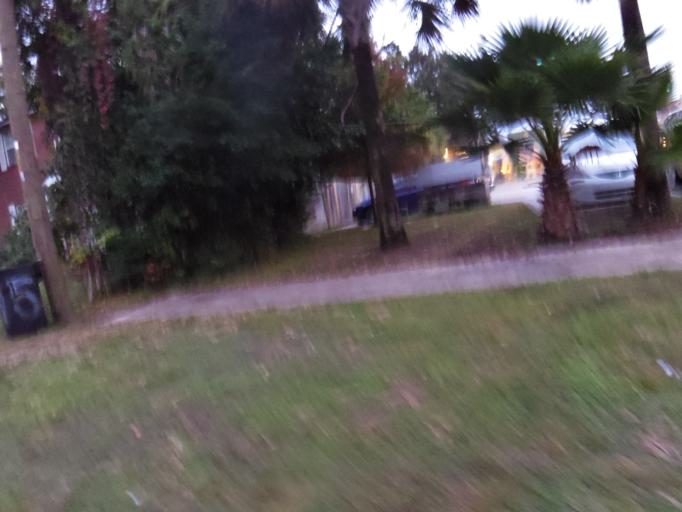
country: US
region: Florida
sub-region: Duval County
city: Jacksonville
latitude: 30.3110
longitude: -81.6558
